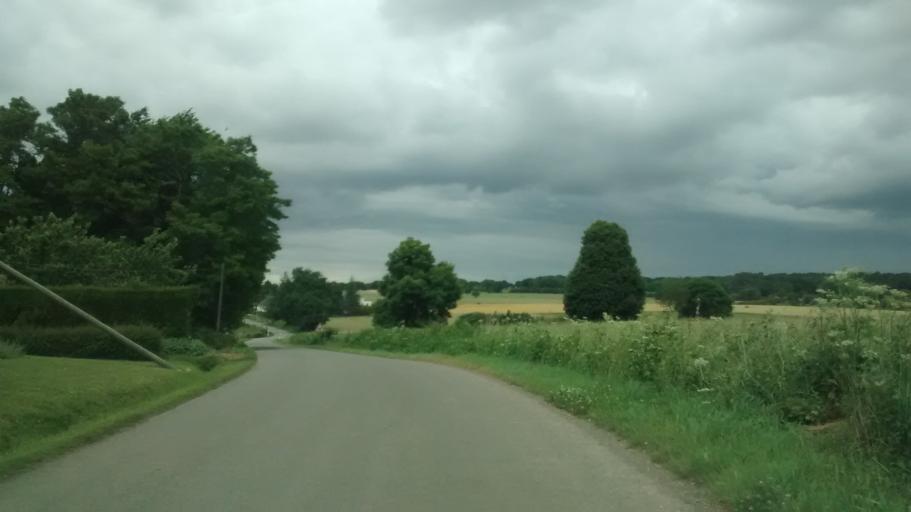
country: FR
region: Brittany
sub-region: Departement d'Ille-et-Vilaine
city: Sixt-sur-Aff
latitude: 47.7930
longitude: -2.1057
